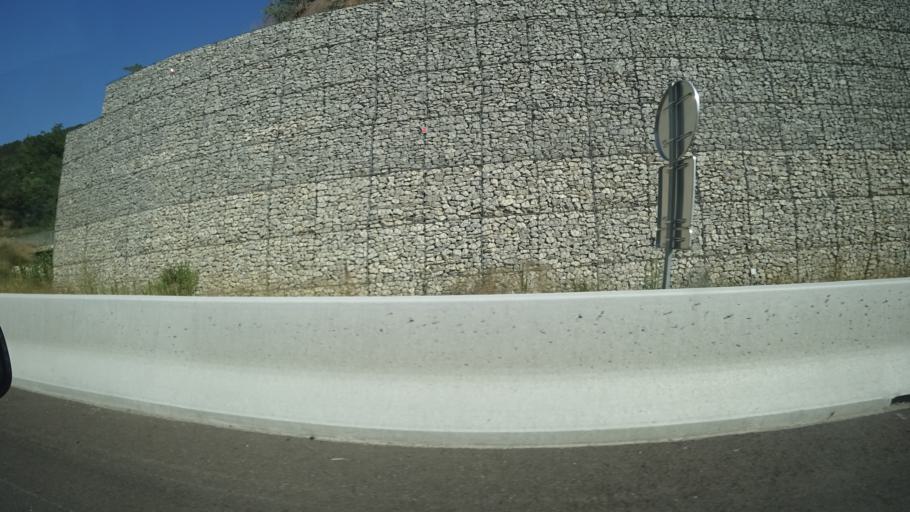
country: FR
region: Languedoc-Roussillon
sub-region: Departement des Pyrenees-Orientales
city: Vernet-les-Bains
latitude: 42.5652
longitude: 2.3126
